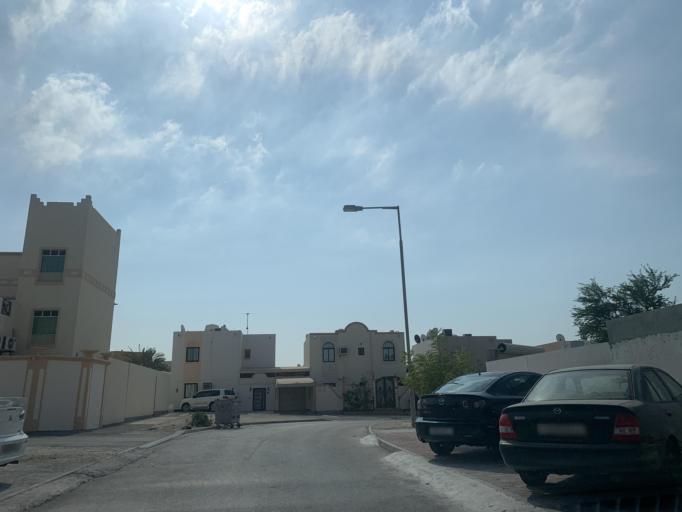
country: BH
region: Central Governorate
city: Madinat Hamad
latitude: 26.1046
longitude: 50.5011
